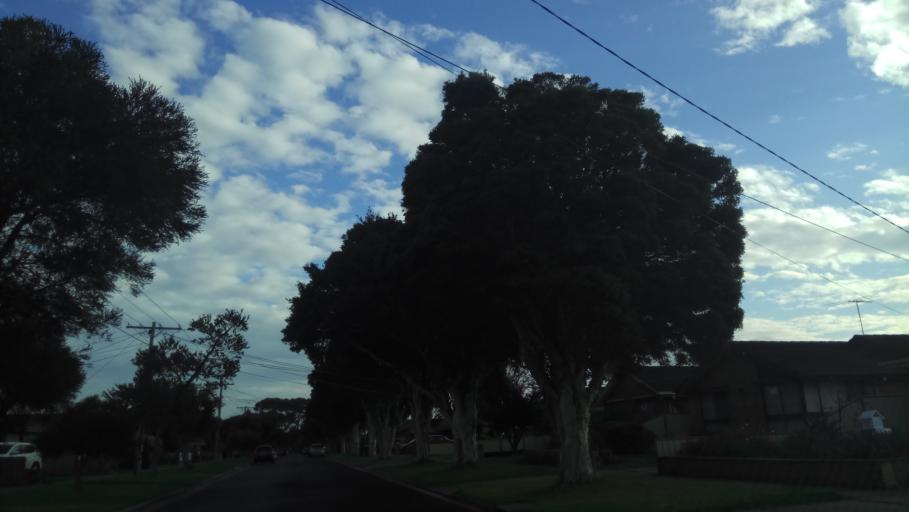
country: AU
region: Victoria
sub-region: Hobsons Bay
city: Laverton
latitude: -37.8681
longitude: 144.7815
